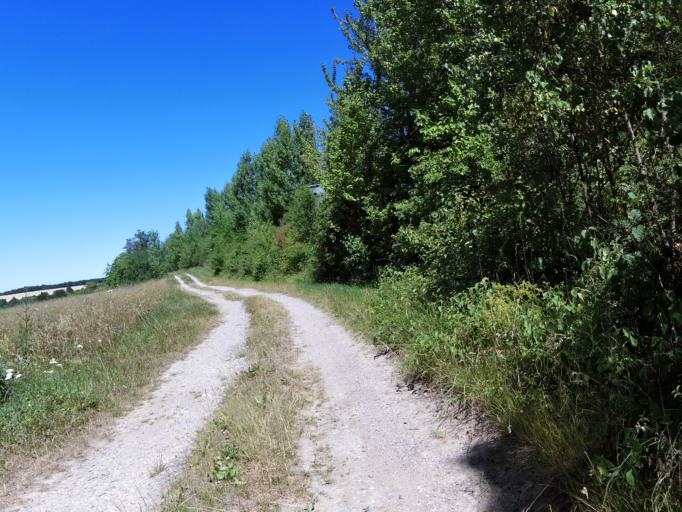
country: DE
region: Bavaria
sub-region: Regierungsbezirk Unterfranken
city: Gerbrunn
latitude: 49.7693
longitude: 9.9999
